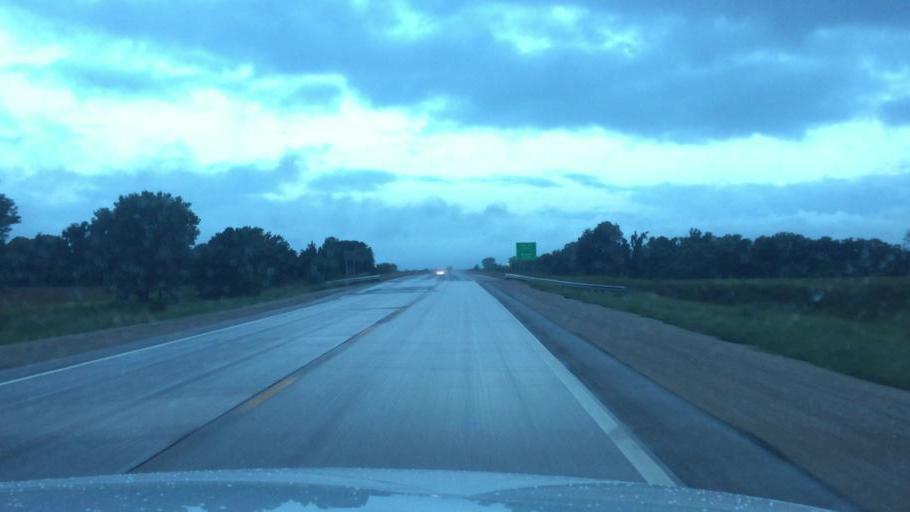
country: US
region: Kansas
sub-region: Neosho County
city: Chanute
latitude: 37.7343
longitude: -95.4567
